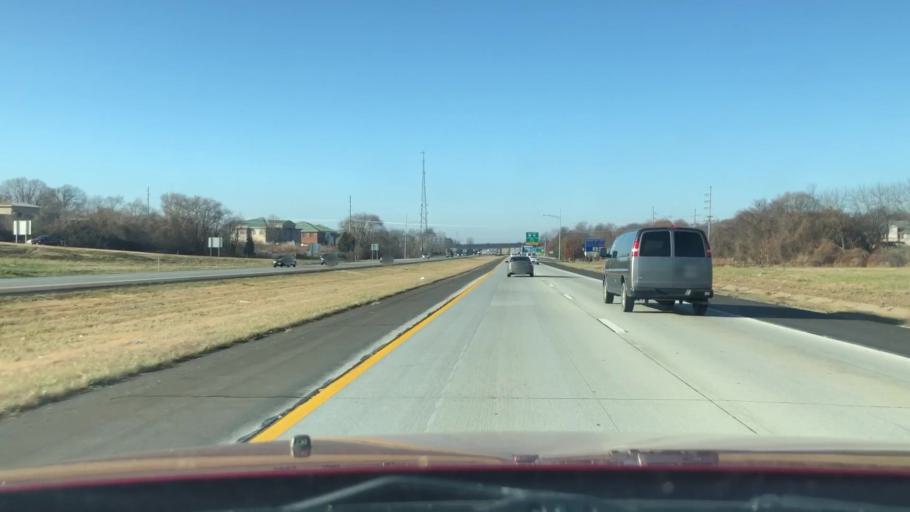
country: US
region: Missouri
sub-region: Greene County
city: Springfield
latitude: 37.1415
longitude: -93.2801
